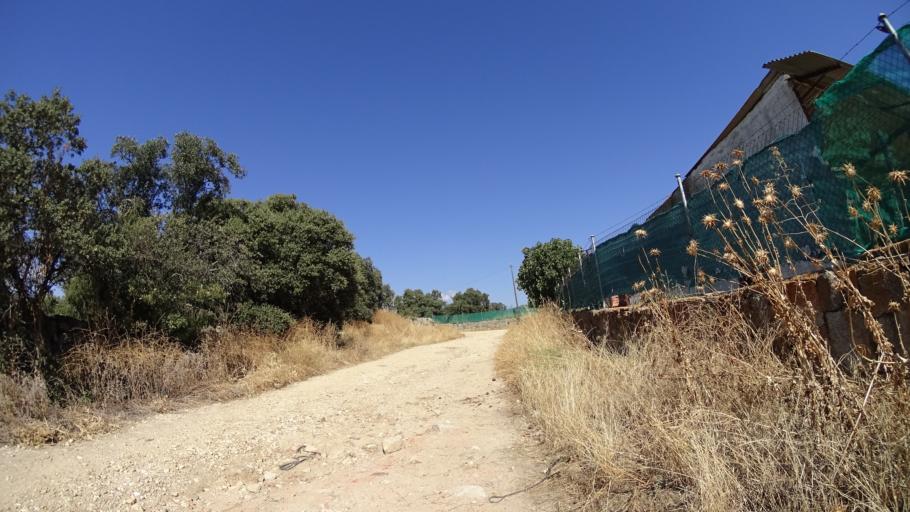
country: ES
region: Madrid
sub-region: Provincia de Madrid
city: Collado-Villalba
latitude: 40.6120
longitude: -4.0033
